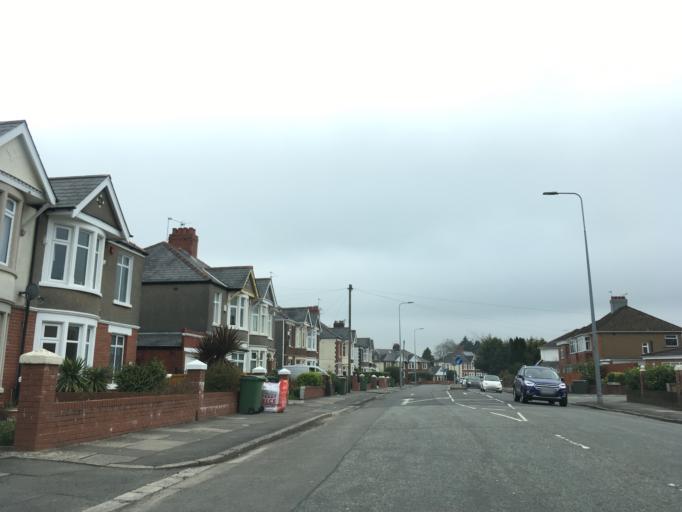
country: GB
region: Wales
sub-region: Cardiff
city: Cardiff
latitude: 51.5189
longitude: -3.1892
